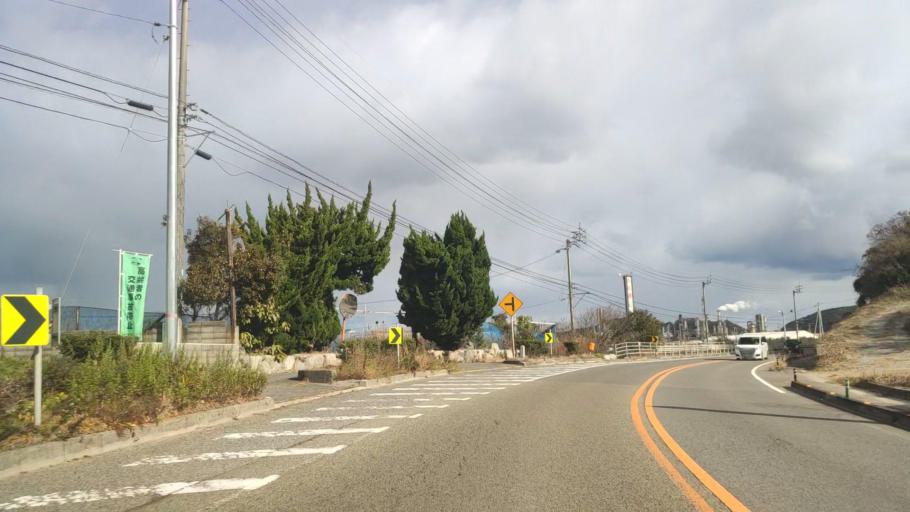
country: JP
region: Ehime
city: Hojo
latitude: 34.0433
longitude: 132.8493
